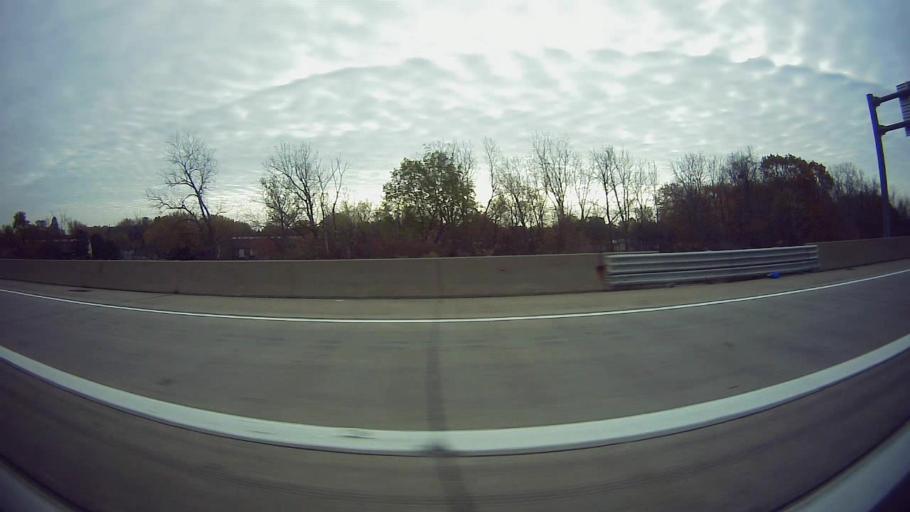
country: US
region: Michigan
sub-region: Wayne County
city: Southgate
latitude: 42.2045
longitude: -83.2327
